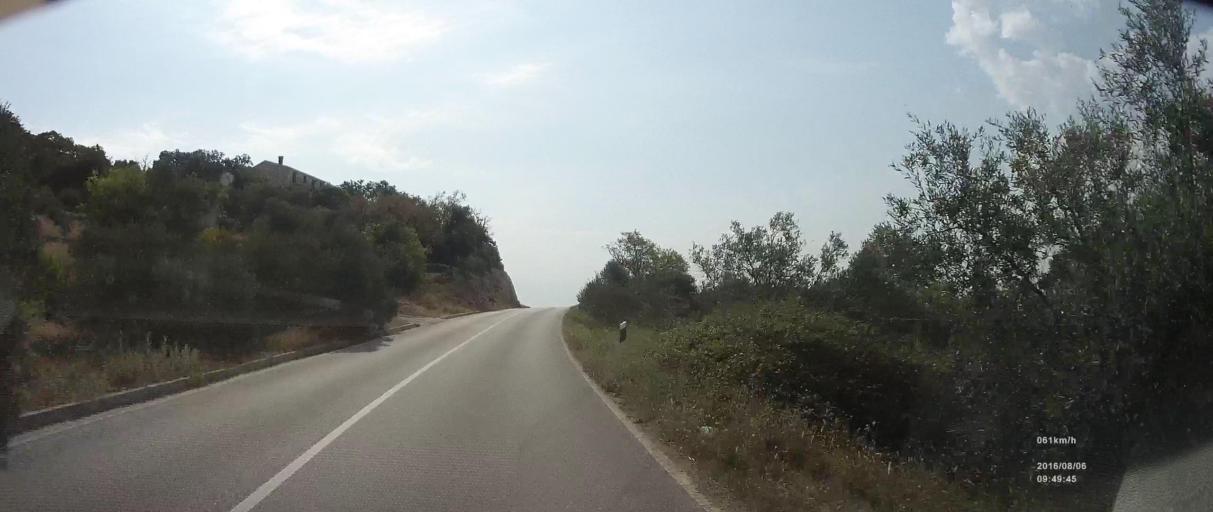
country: HR
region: Dubrovacko-Neretvanska
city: Blato
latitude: 42.7362
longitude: 17.5450
